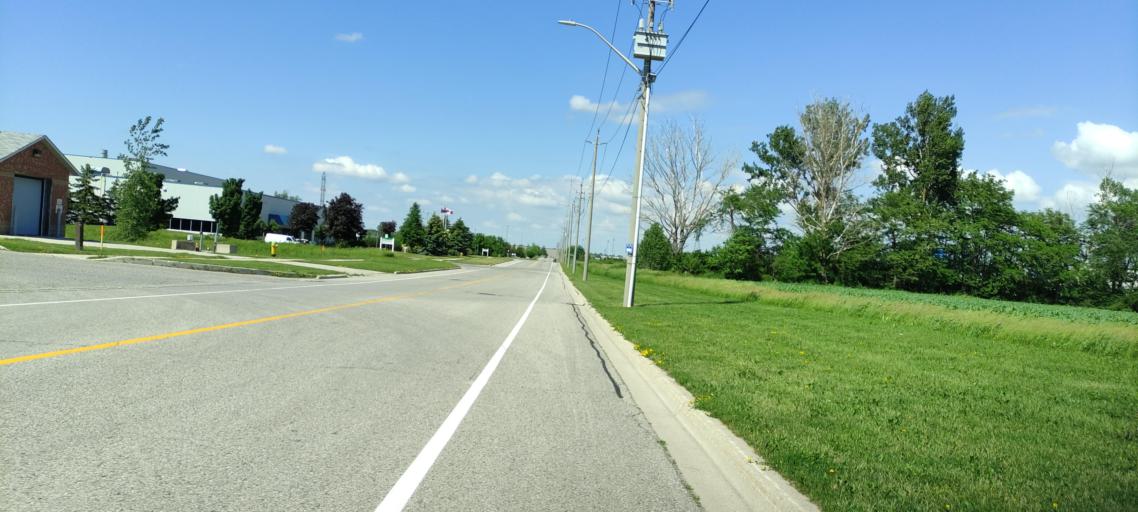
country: CA
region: Ontario
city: Stratford
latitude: 43.3432
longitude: -81.0124
